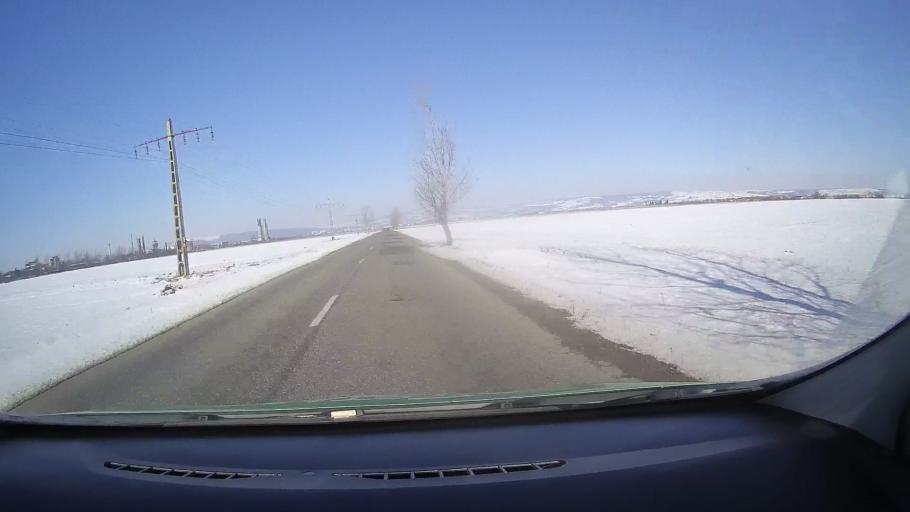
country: RO
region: Brasov
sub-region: Comuna Harseni
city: Harseni
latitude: 45.7999
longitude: 24.9932
